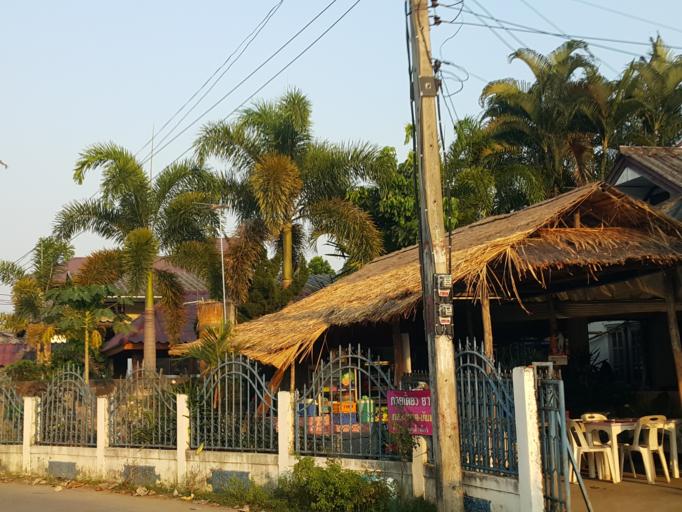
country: TH
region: Chiang Mai
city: San Sai
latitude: 18.8969
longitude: 98.9500
